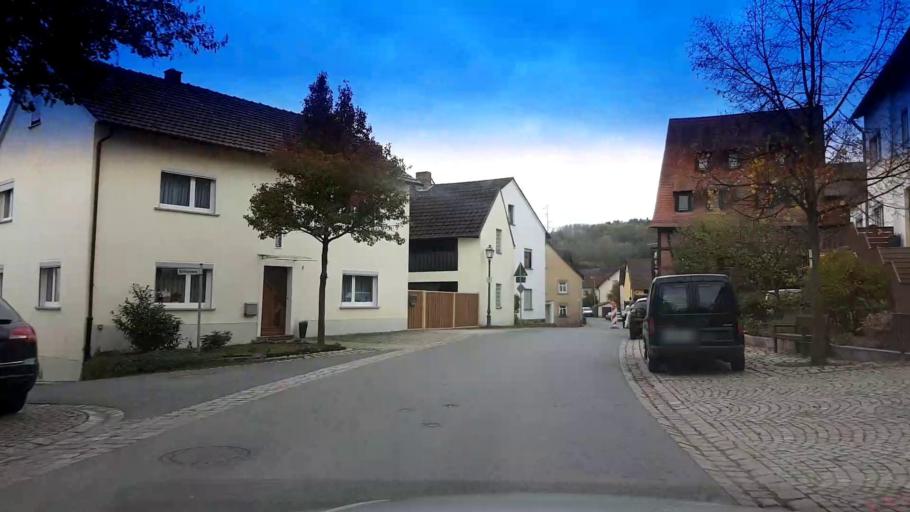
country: DE
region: Bavaria
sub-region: Upper Franconia
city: Viereth-Trunstadt
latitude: 49.9226
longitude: 10.7771
